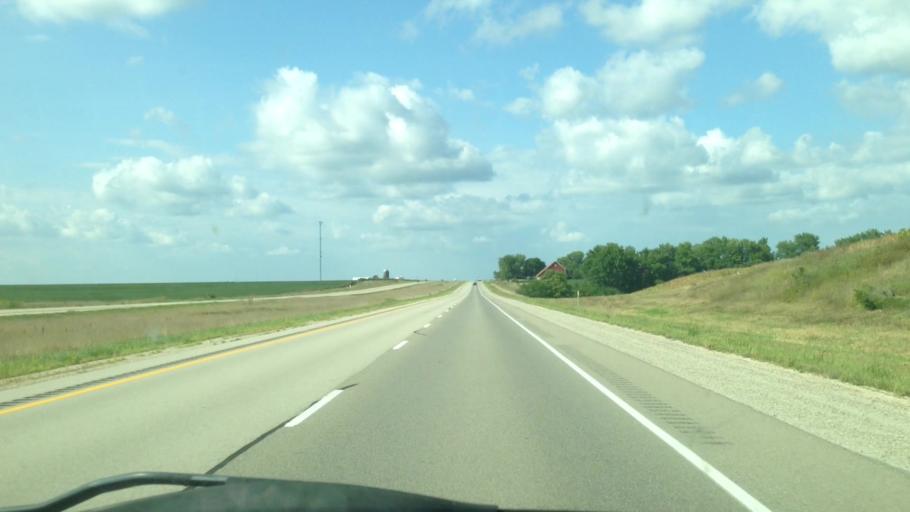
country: US
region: Iowa
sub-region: Henry County
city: Mount Pleasant
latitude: 40.8034
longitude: -91.5642
